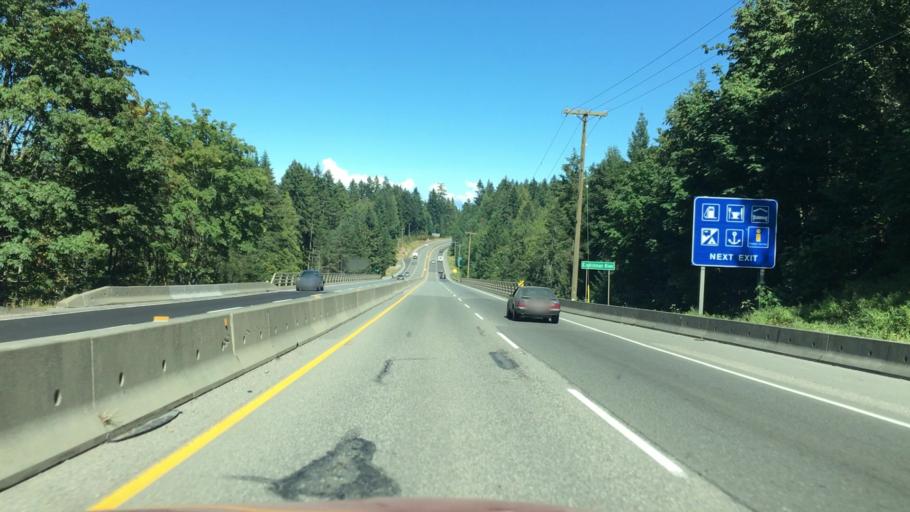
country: CA
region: British Columbia
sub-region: Regional District of Nanaimo
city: Parksville
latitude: 49.2997
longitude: -124.2754
